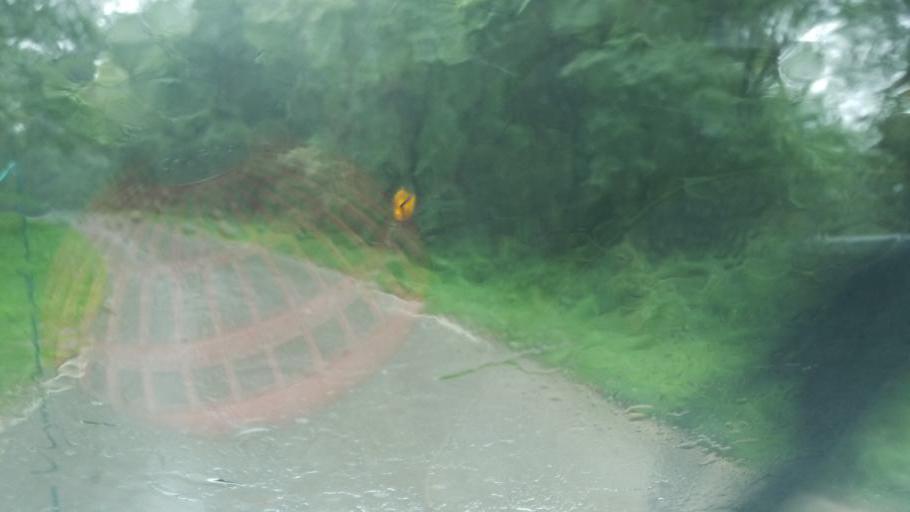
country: US
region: Ohio
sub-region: Adams County
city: Manchester
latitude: 38.5201
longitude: -83.5191
